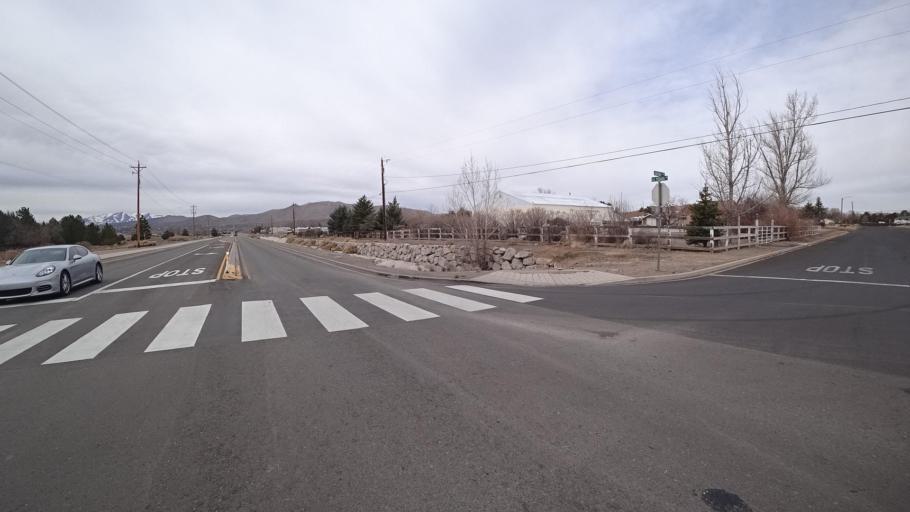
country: US
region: Nevada
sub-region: Washoe County
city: Spanish Springs
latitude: 39.6362
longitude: -119.6914
